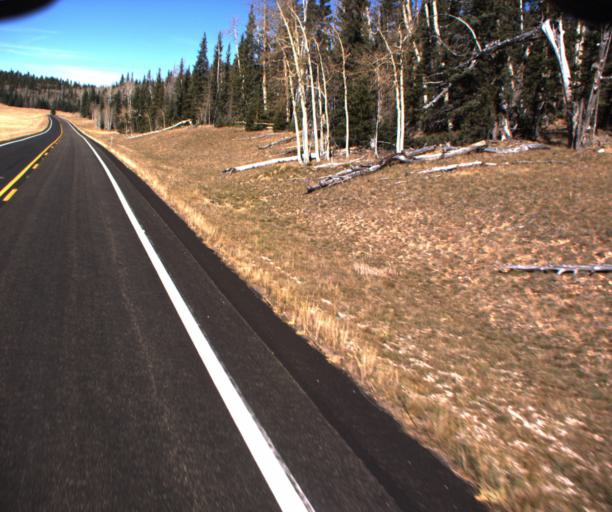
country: US
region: Arizona
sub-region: Coconino County
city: Grand Canyon
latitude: 36.4351
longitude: -112.1337
